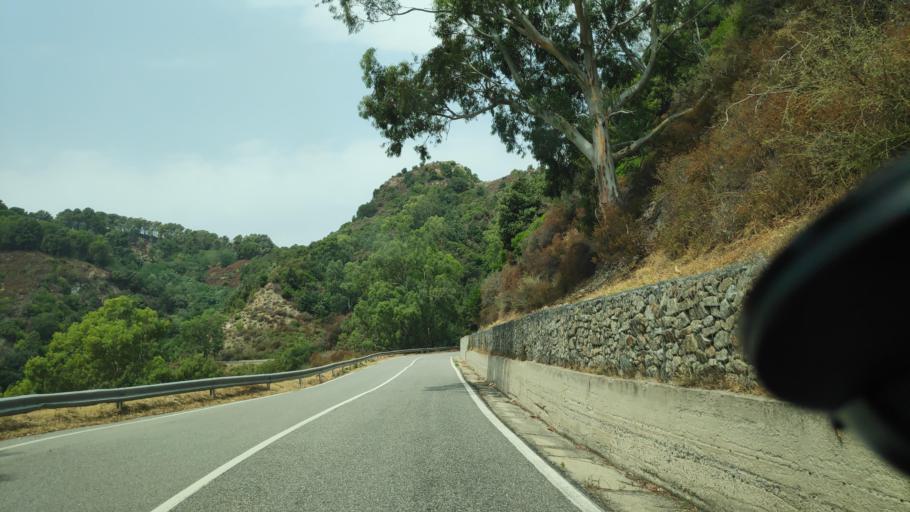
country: IT
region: Calabria
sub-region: Provincia di Catanzaro
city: San Sostene
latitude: 38.6401
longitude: 16.5113
